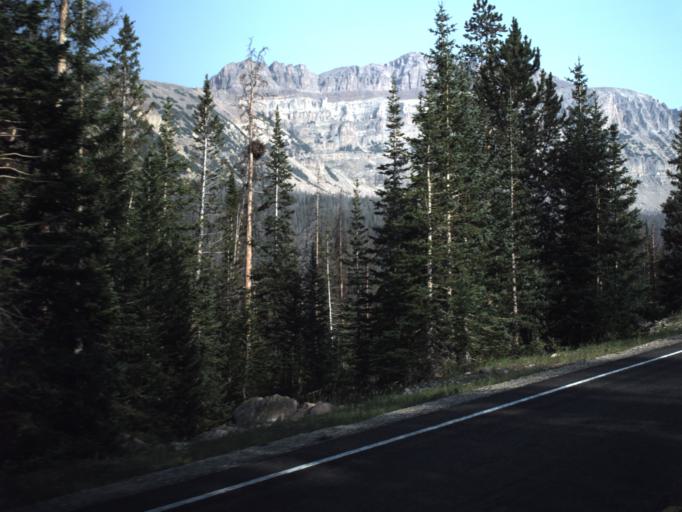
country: US
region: Utah
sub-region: Summit County
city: Kamas
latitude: 40.7459
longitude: -110.8733
